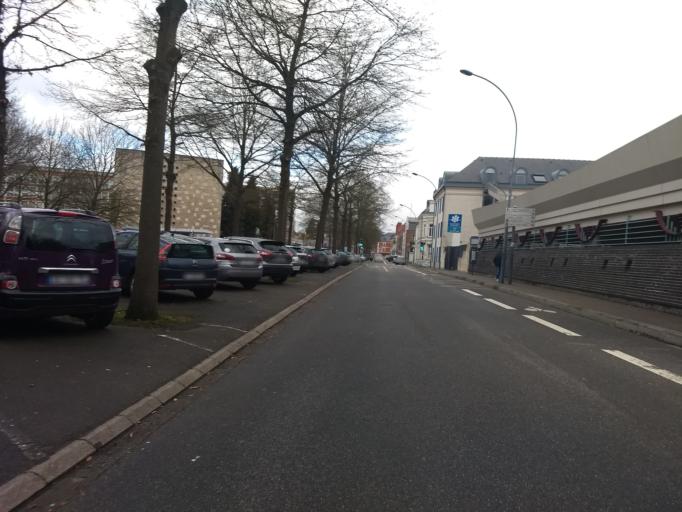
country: FR
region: Nord-Pas-de-Calais
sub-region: Departement du Pas-de-Calais
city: Achicourt
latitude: 50.2867
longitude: 2.7669
